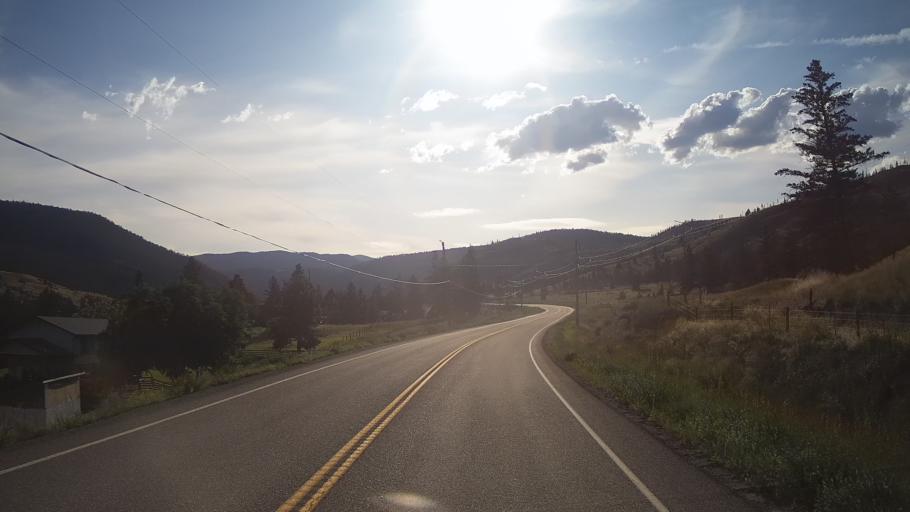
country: CA
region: British Columbia
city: Cache Creek
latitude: 50.8868
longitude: -121.4591
